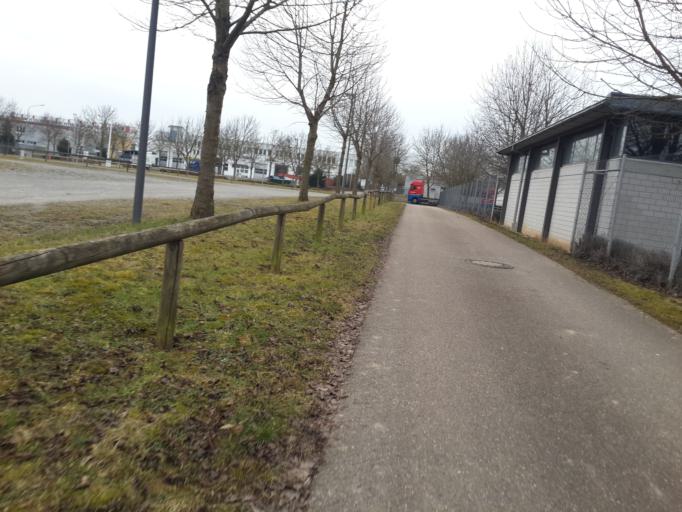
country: DE
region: Baden-Wuerttemberg
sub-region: Regierungsbezirk Stuttgart
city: Untereisesheim
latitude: 49.1850
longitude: 9.1698
